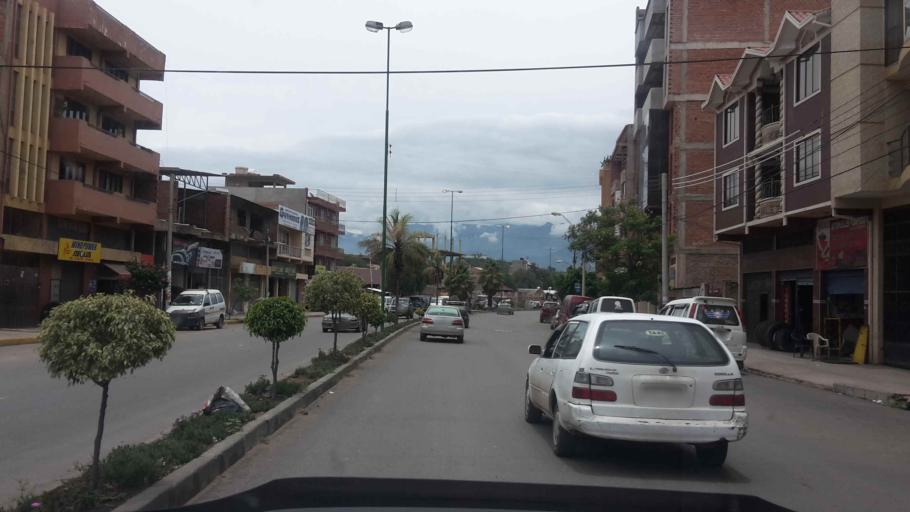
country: BO
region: Cochabamba
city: Cochabamba
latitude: -17.4159
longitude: -66.1527
